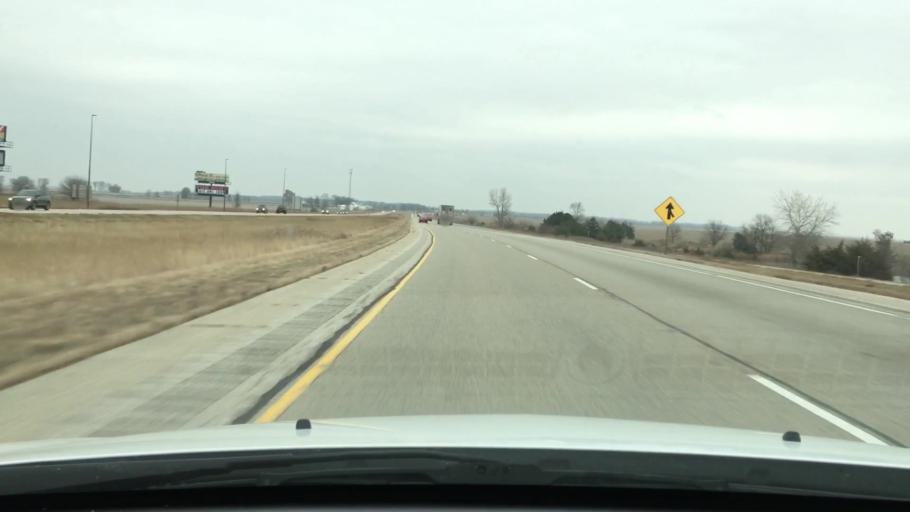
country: US
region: Illinois
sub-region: Logan County
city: Atlanta
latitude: 40.3141
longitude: -89.1615
